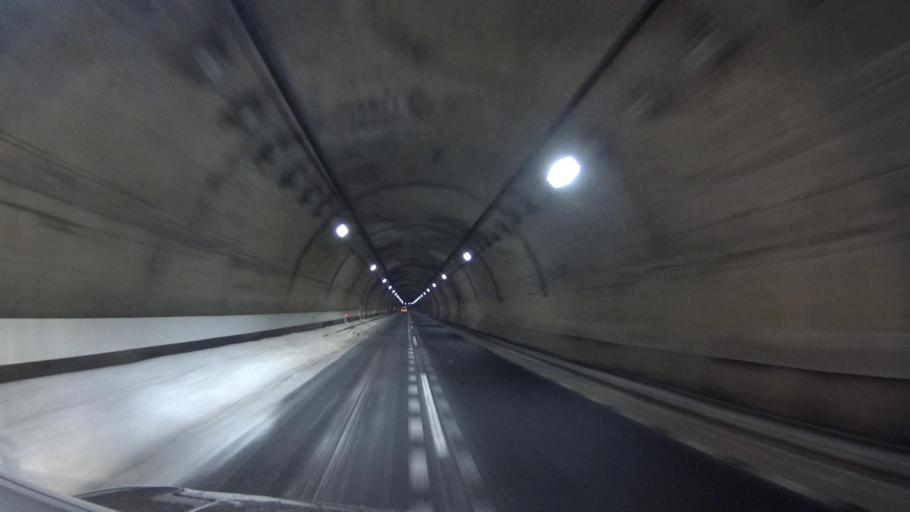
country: JP
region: Hokkaido
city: Otaru
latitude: 43.1658
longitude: 141.0936
